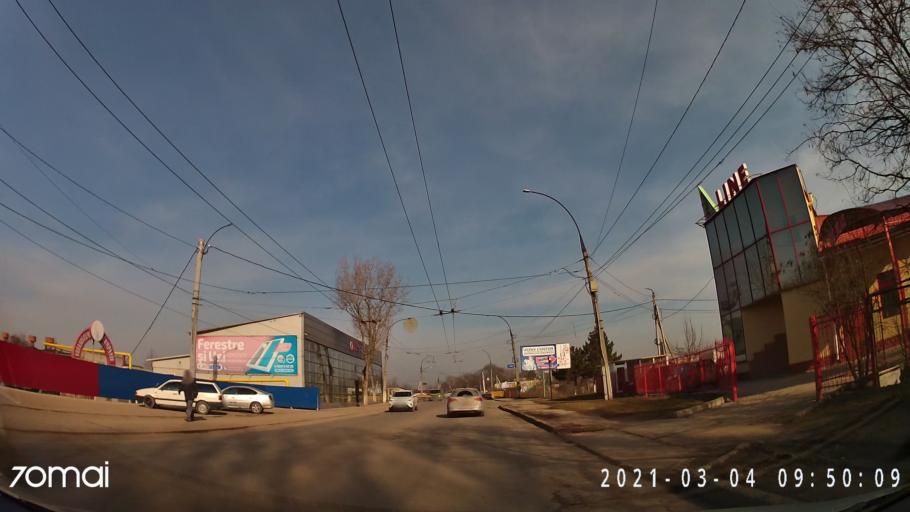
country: MD
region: Balti
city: Balti
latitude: 47.7701
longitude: 27.9299
